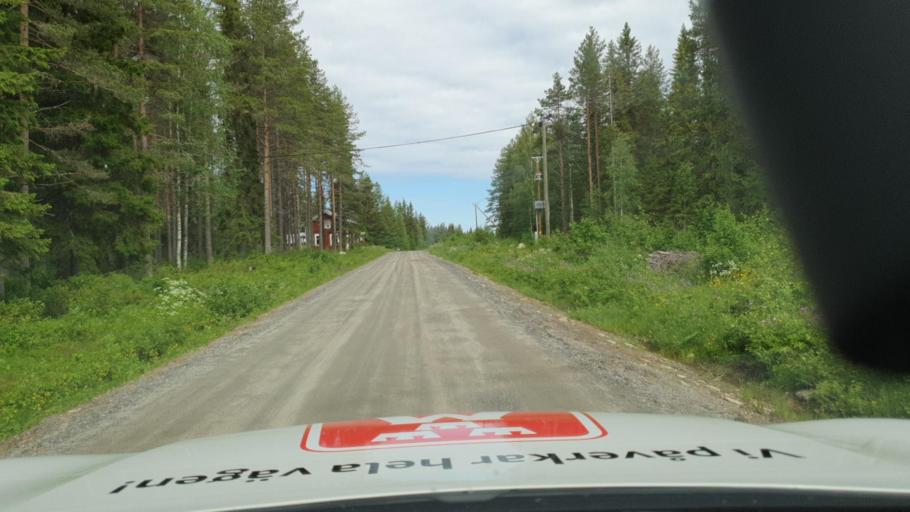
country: SE
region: Vaesterbotten
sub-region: Skelleftea Kommun
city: Langsele
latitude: 64.5756
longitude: 20.2968
